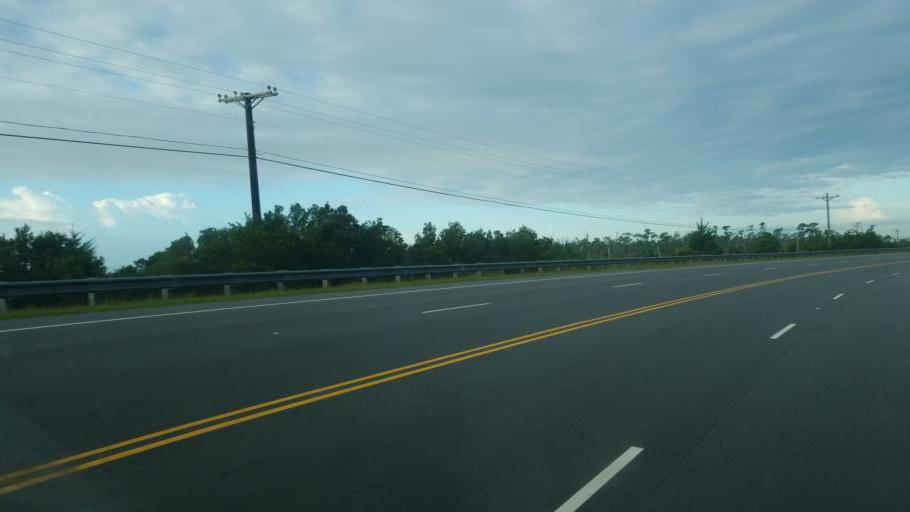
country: US
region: North Carolina
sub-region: Dare County
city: Manteo
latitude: 35.8725
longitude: -75.7832
